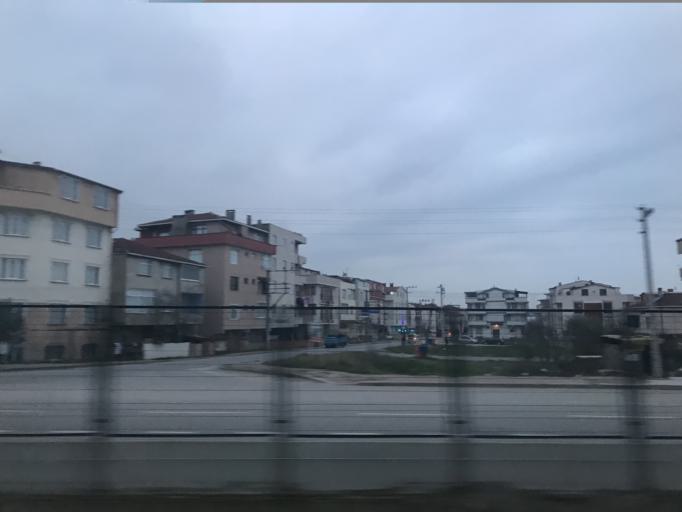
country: TR
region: Kocaeli
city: Darica
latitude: 40.7924
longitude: 29.3902
